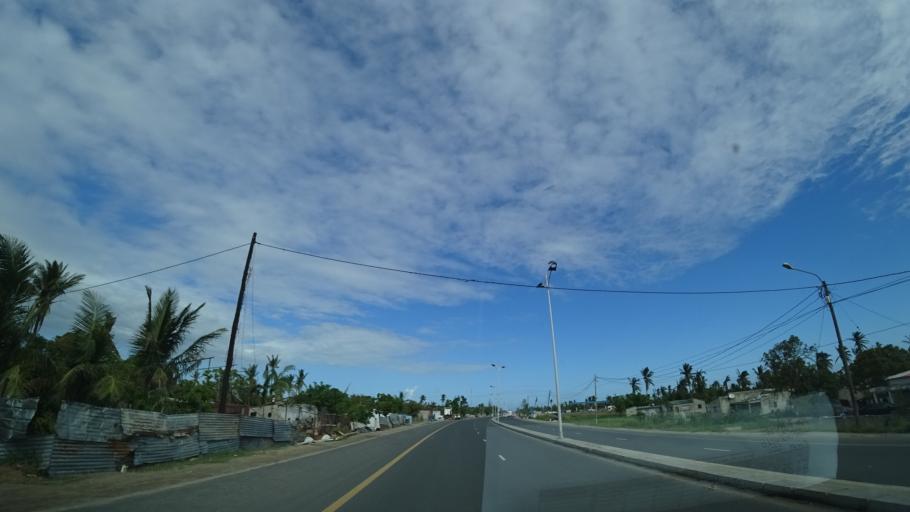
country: MZ
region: Sofala
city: Beira
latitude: -19.7515
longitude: 34.8756
